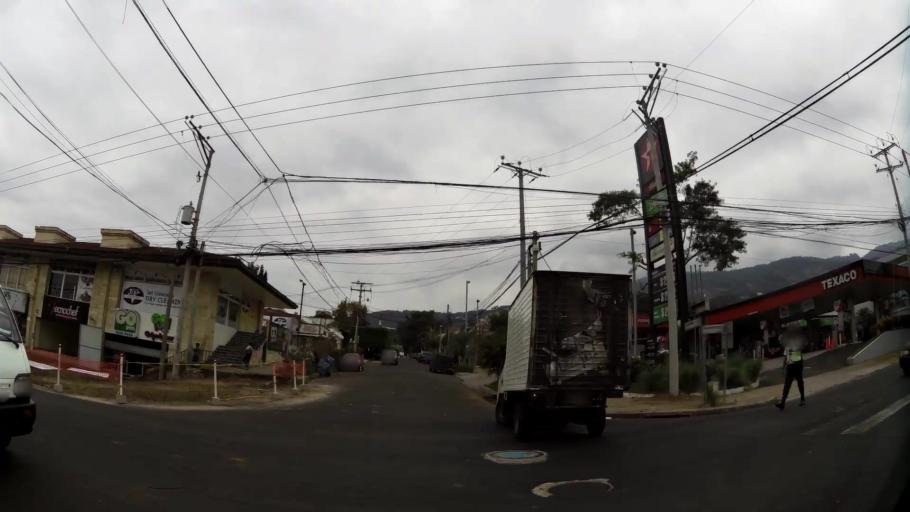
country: SV
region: La Libertad
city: Antiguo Cuscatlan
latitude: 13.7052
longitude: -89.2493
